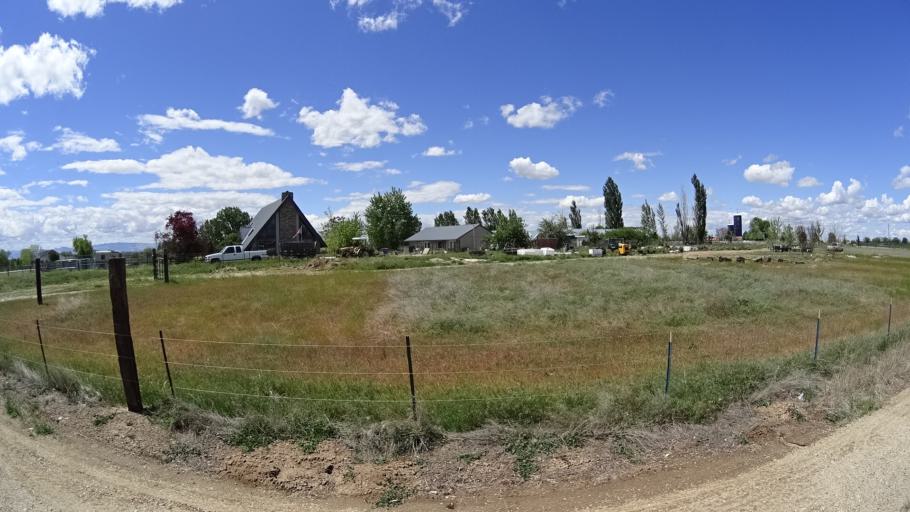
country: US
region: Idaho
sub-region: Ada County
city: Kuna
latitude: 43.5595
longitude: -116.4536
